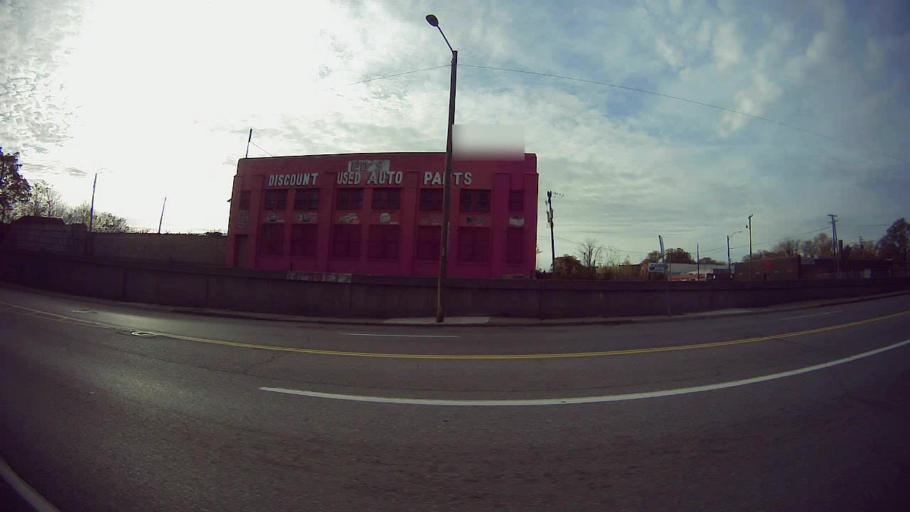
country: US
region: Michigan
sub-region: Wayne County
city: Highland Park
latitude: 42.4323
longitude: -83.1018
